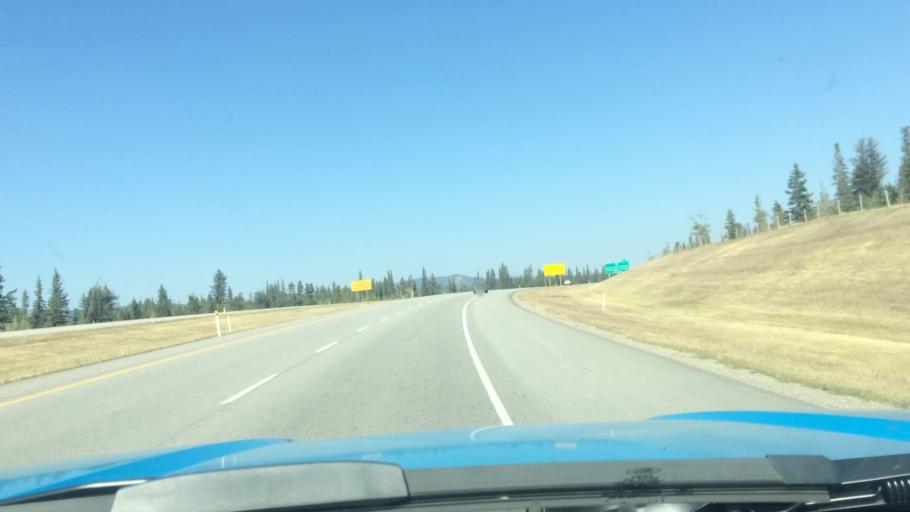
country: CA
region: Alberta
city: Canmore
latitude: 51.0882
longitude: -115.0536
